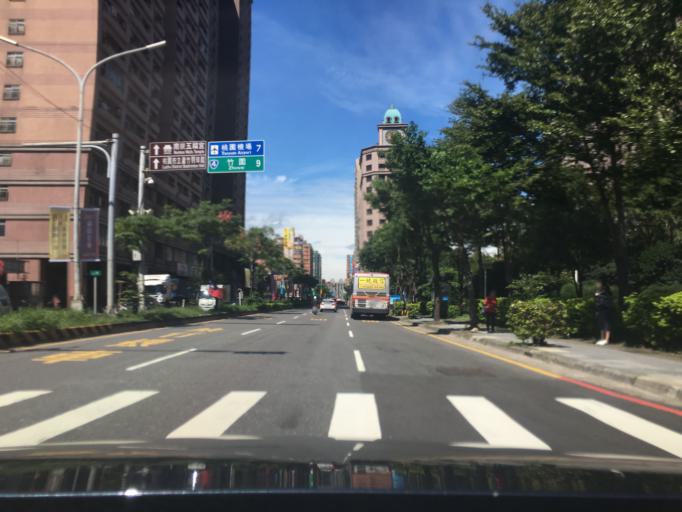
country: TW
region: Taiwan
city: Taoyuan City
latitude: 25.0417
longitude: 121.2954
